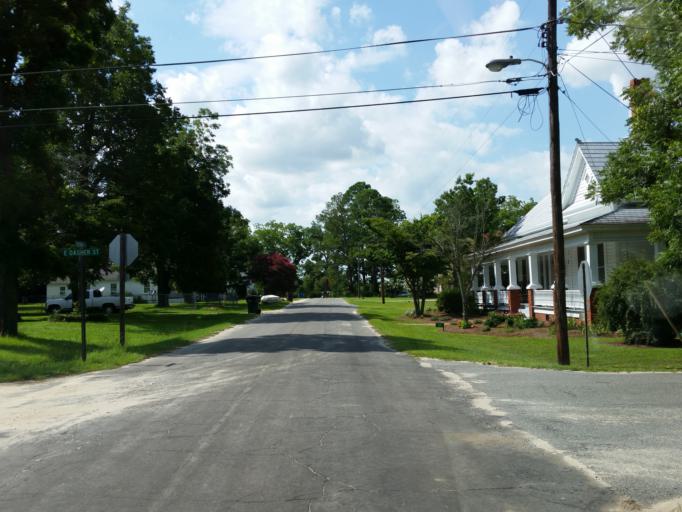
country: US
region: Georgia
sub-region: Turner County
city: Ashburn
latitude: 31.6710
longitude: -83.6313
